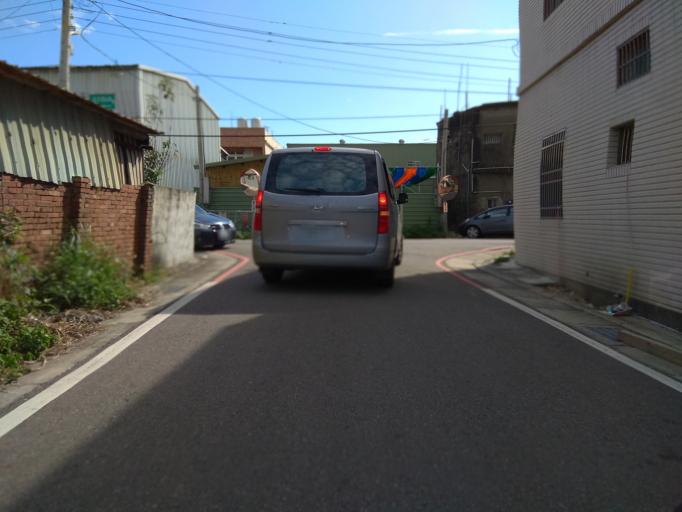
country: TW
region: Taiwan
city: Taoyuan City
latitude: 25.0471
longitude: 121.1402
